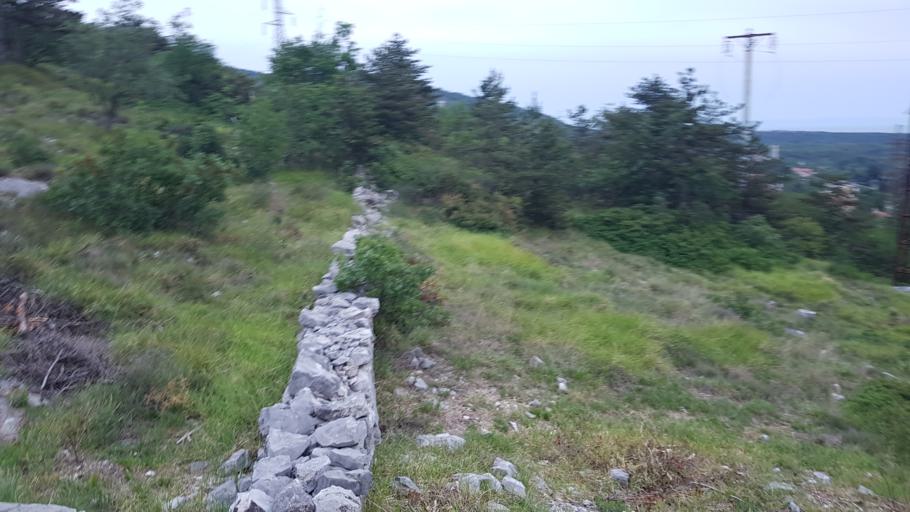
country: IT
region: Friuli Venezia Giulia
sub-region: Provincia di Trieste
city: Duino
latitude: 45.7958
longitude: 13.5900
